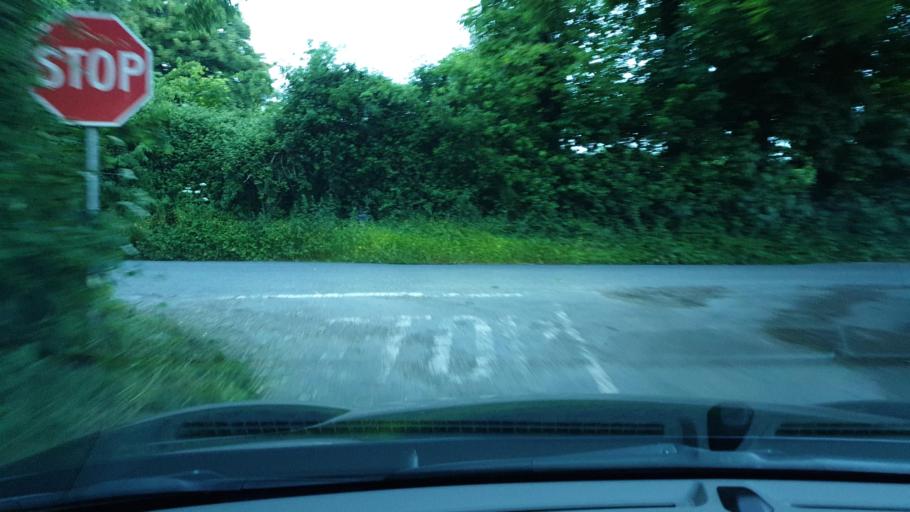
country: IE
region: Leinster
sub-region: An Mhi
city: Duleek
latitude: 53.5920
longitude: -6.3665
